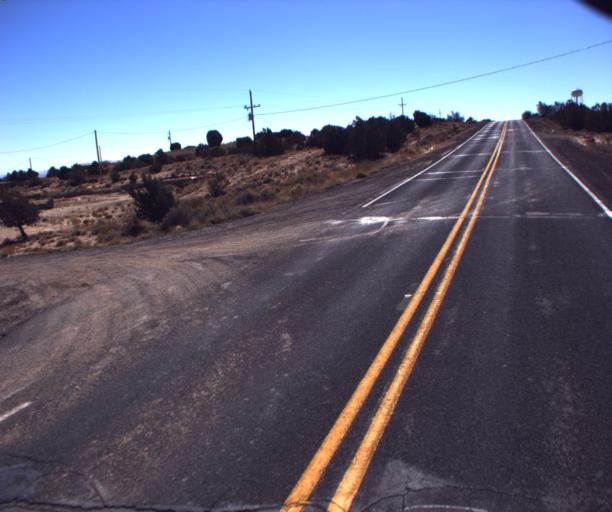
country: US
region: Arizona
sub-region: Navajo County
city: First Mesa
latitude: 35.8264
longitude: -110.5325
